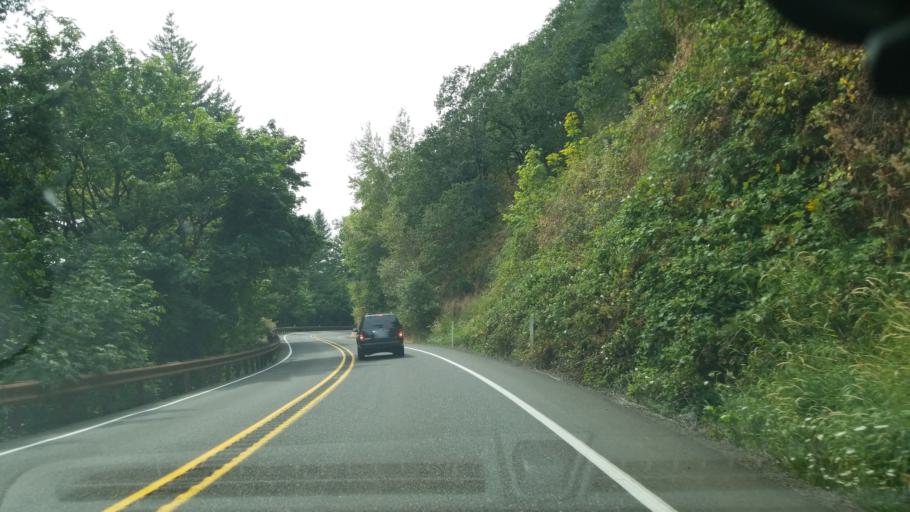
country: US
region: Washington
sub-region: Clark County
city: Washougal
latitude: 45.5597
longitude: -122.2462
